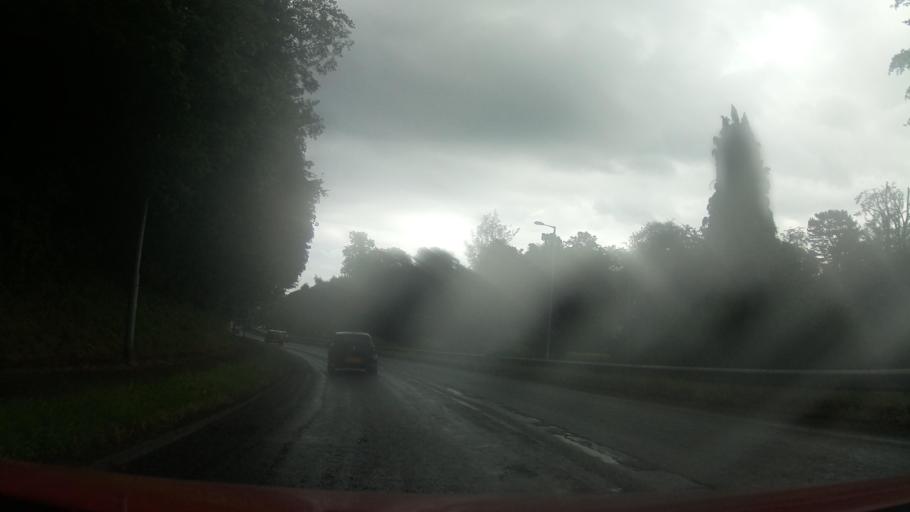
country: GB
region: England
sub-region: Dudley
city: Kingswinford
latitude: 52.5538
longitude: -2.1729
